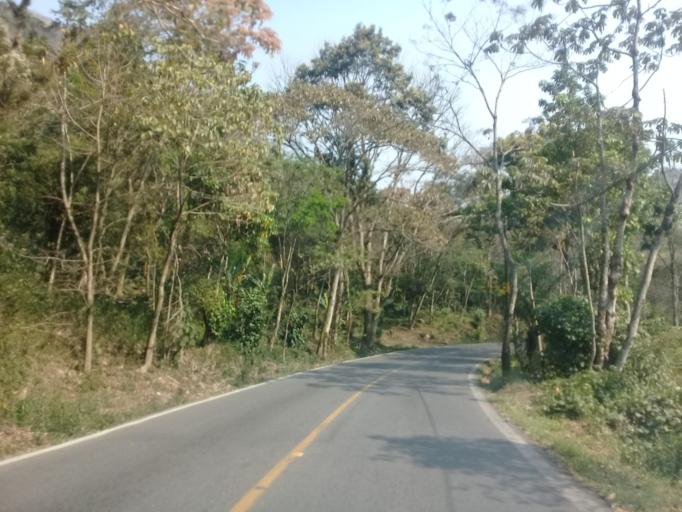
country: MX
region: Veracruz
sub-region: Ixtaczoquitlan
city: Campo Chico
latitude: 18.8410
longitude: -97.0237
